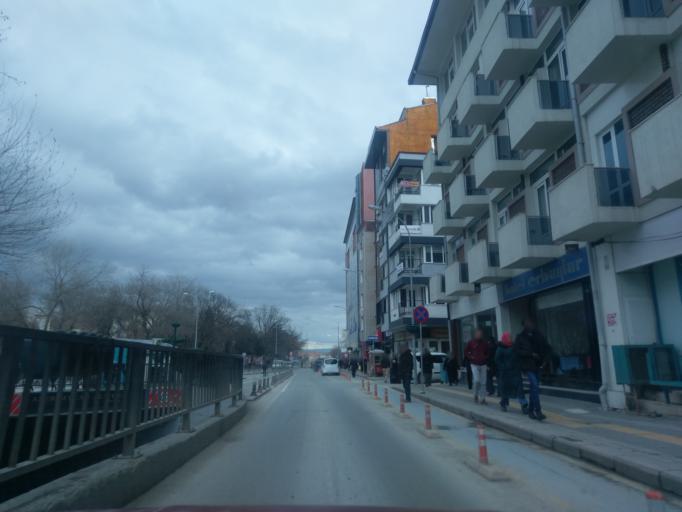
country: TR
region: Kuetahya
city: Kutahya
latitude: 39.4189
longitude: 29.9868
